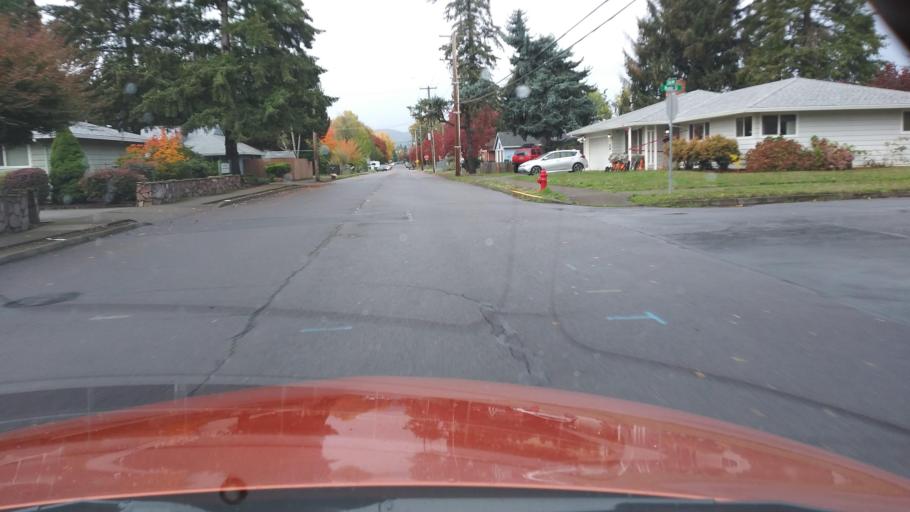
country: US
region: Oregon
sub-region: Washington County
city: Forest Grove
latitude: 45.5224
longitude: -123.0908
